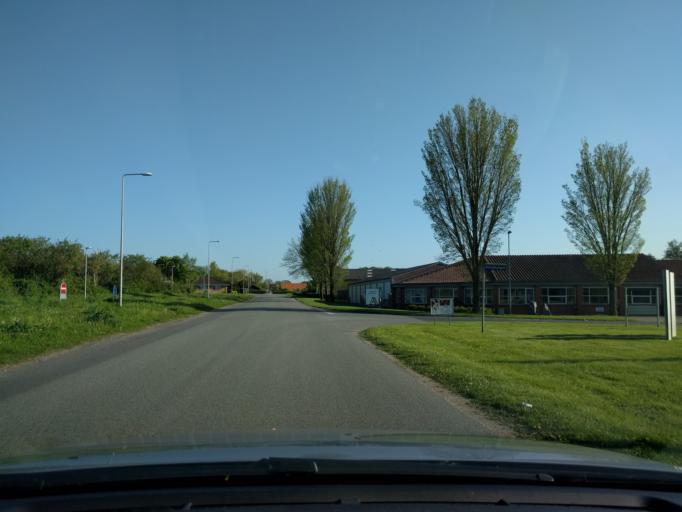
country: DK
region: South Denmark
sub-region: Kerteminde Kommune
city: Kerteminde
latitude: 55.4597
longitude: 10.6565
